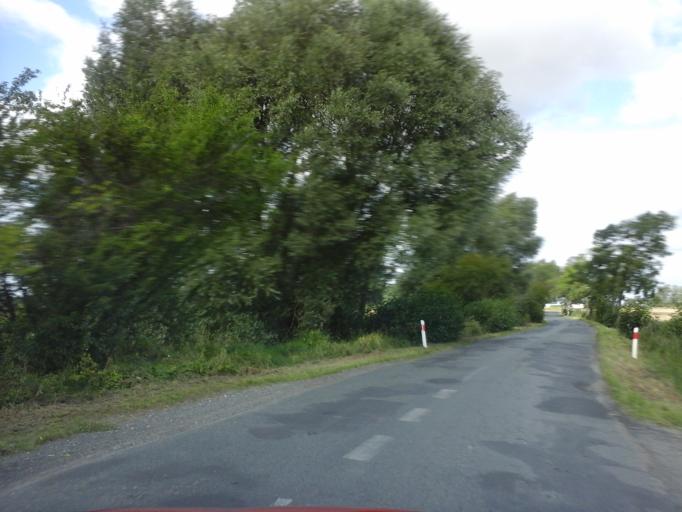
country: PL
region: West Pomeranian Voivodeship
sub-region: Powiat stargardzki
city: Kobylanka
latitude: 53.3156
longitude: 14.9357
